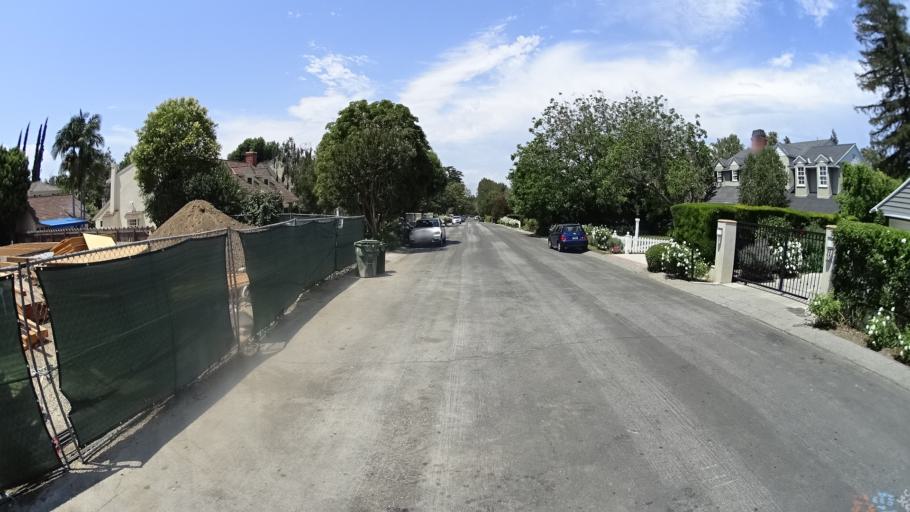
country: US
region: California
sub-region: Los Angeles County
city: Sherman Oaks
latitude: 34.1418
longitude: -118.4198
